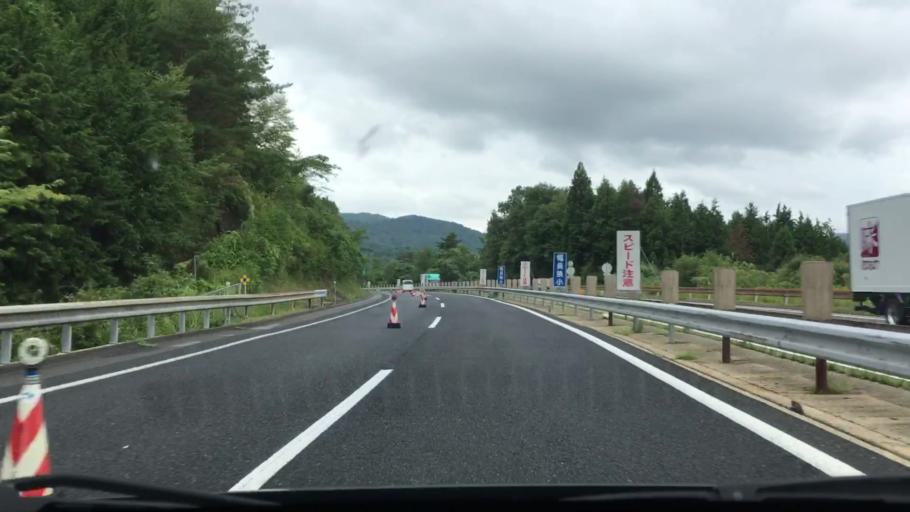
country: JP
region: Hiroshima
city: Miyoshi
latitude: 34.7334
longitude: 132.7069
